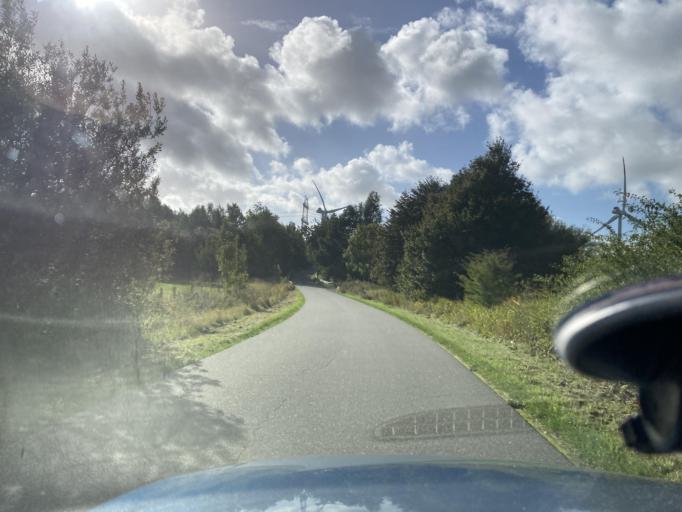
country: DE
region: Schleswig-Holstein
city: Lohe-Rickelshof
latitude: 54.1829
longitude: 9.0555
